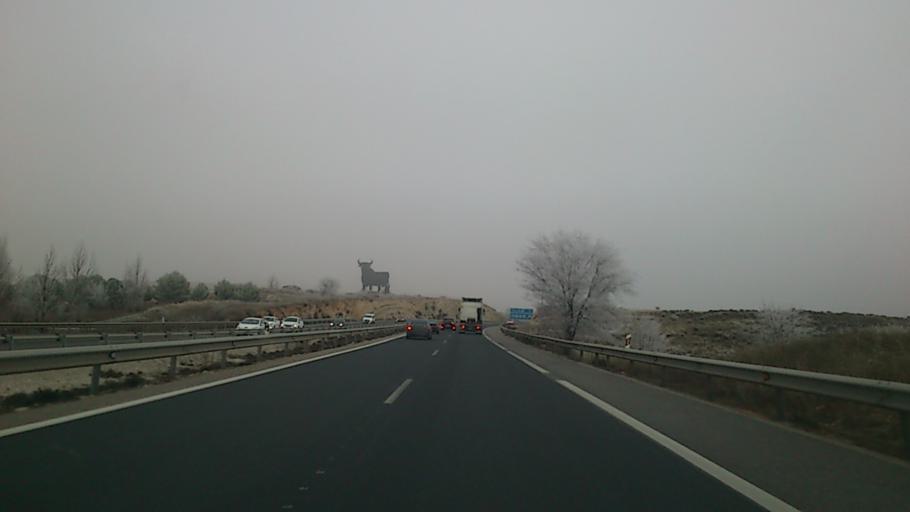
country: ES
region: Castille-La Mancha
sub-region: Provincia de Guadalajara
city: Torremocha del Campo
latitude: 40.9671
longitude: -2.6331
